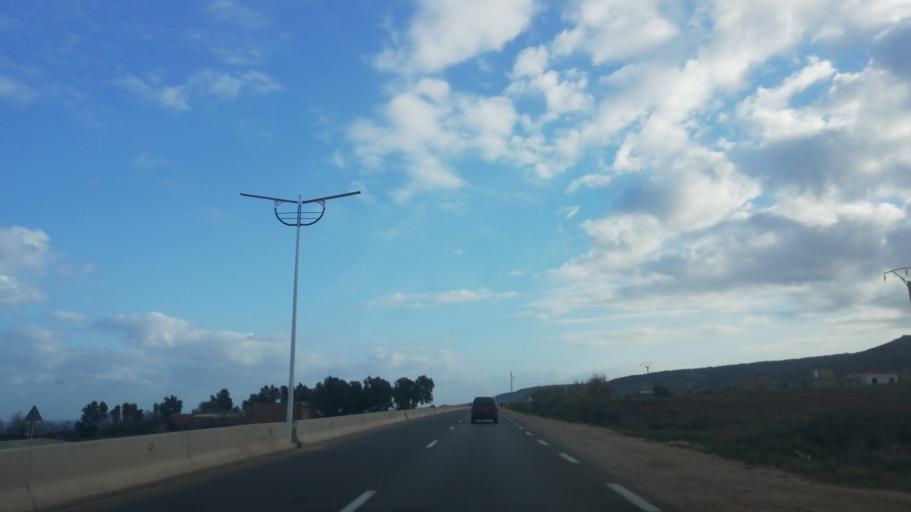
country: DZ
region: Mostaganem
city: Mostaganem
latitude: 36.0735
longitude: 0.1798
